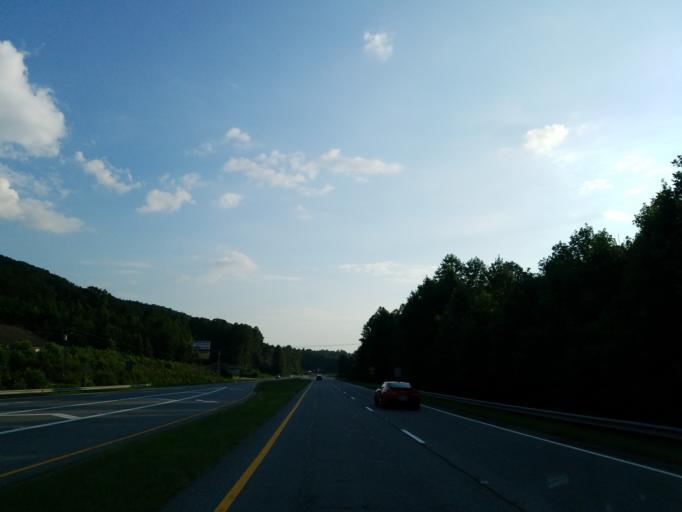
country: US
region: Georgia
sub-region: Fannin County
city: Blue Ridge
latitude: 34.8344
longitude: -84.3440
